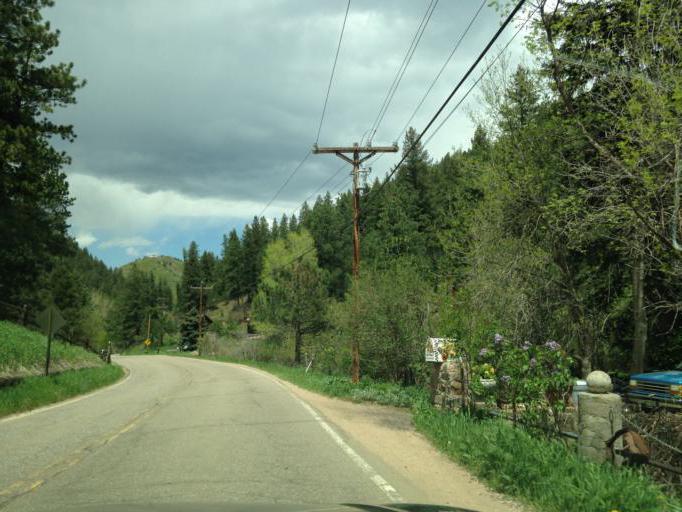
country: US
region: Colorado
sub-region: Jefferson County
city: Ken Caryl
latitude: 39.5236
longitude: -105.1850
